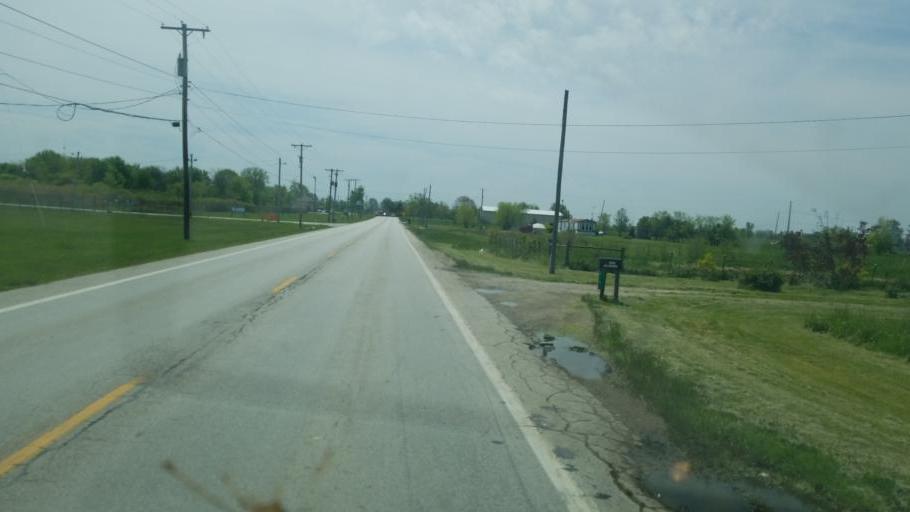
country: US
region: Ohio
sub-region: Ottawa County
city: Oak Harbor
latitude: 41.5915
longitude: -83.0967
